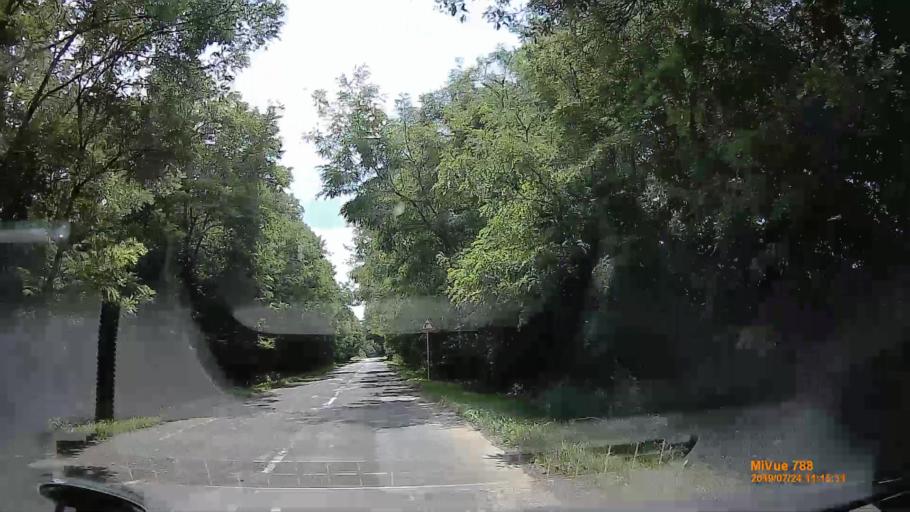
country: HU
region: Szabolcs-Szatmar-Bereg
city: Tarpa
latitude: 48.1903
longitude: 22.4581
